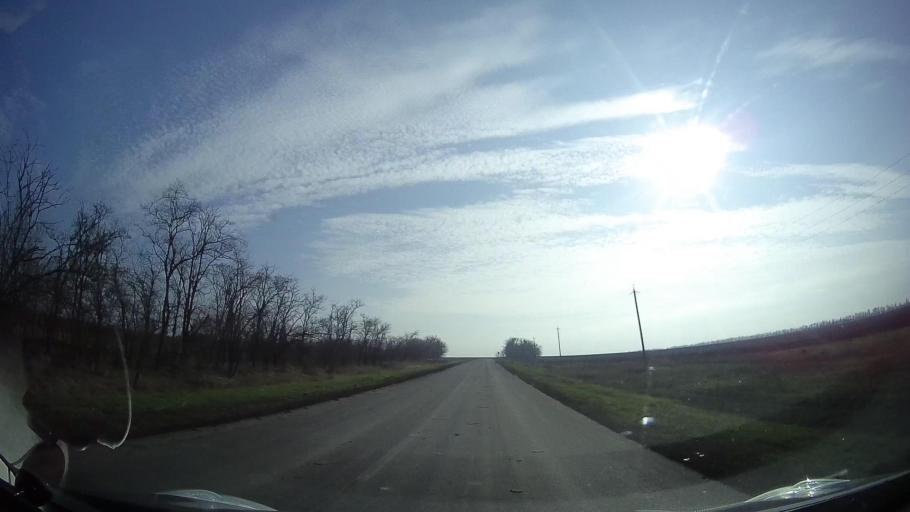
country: RU
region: Rostov
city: Mechetinskaya
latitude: 46.9089
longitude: 40.5357
